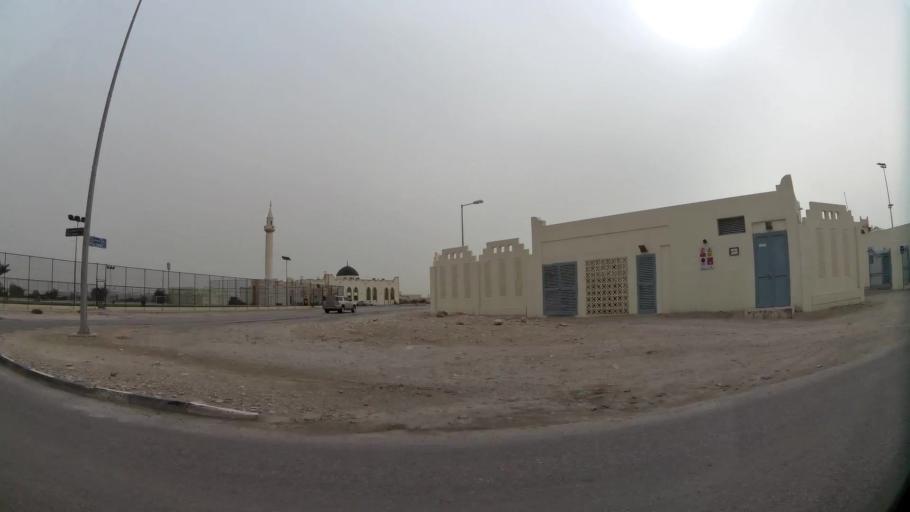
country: QA
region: Baladiyat ad Dawhah
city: Doha
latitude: 25.2429
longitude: 51.5109
